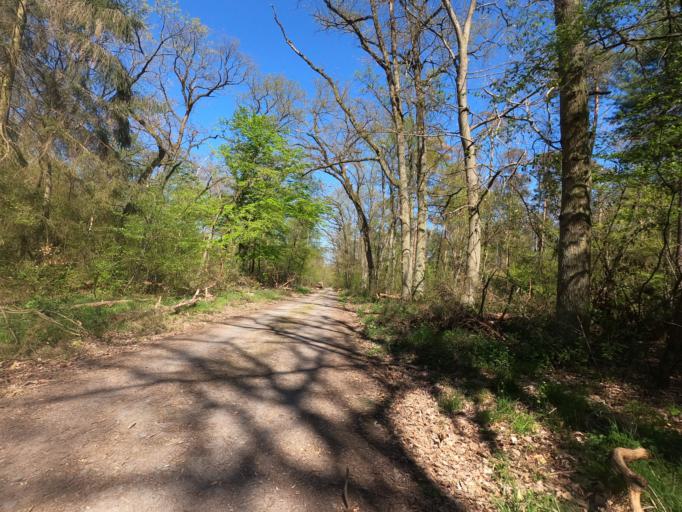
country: DE
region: Hesse
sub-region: Regierungsbezirk Darmstadt
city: Buttelborn
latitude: 49.9325
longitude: 8.5176
